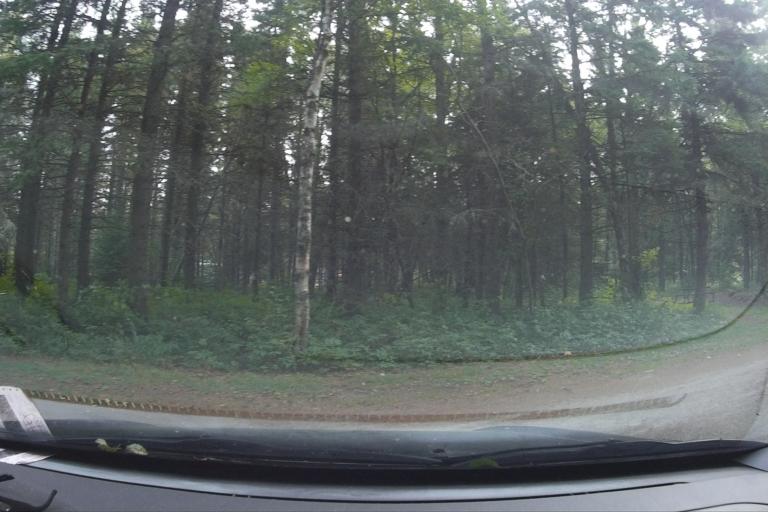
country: CA
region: Ontario
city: Marathon
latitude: 48.7879
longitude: -86.6271
